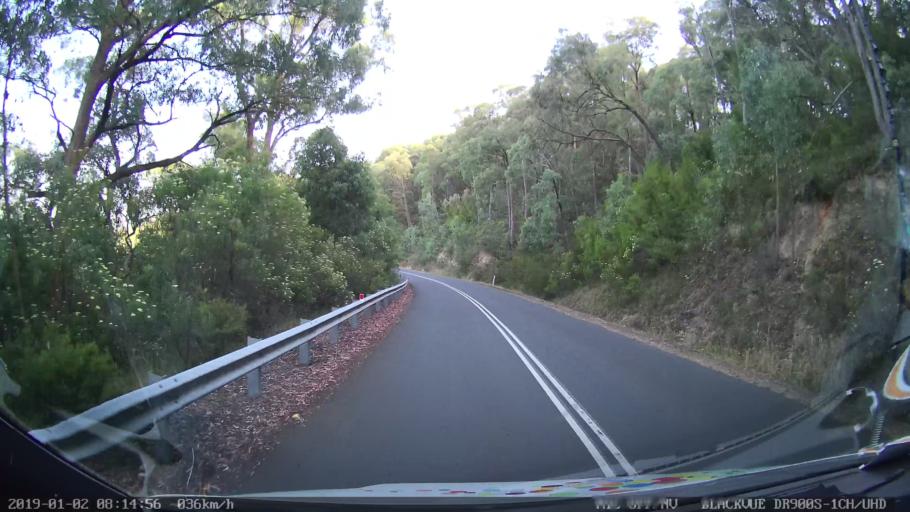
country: AU
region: New South Wales
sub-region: Tumut Shire
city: Tumut
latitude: -35.5844
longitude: 148.3400
